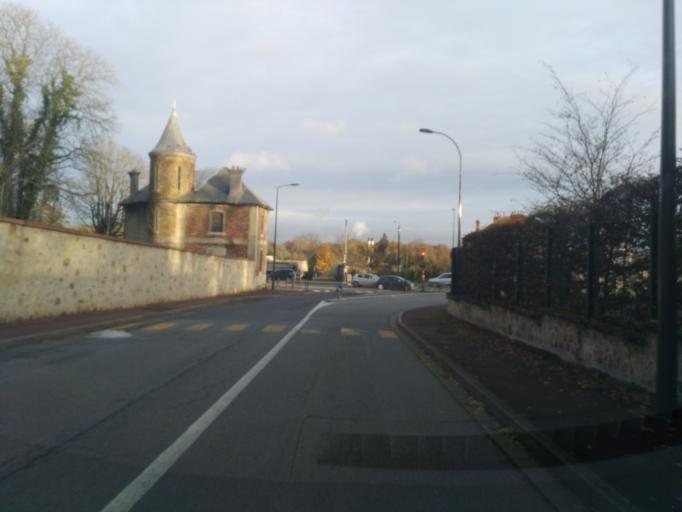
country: FR
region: Ile-de-France
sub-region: Departement des Yvelines
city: Fourqueux
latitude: 48.9005
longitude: 2.0629
